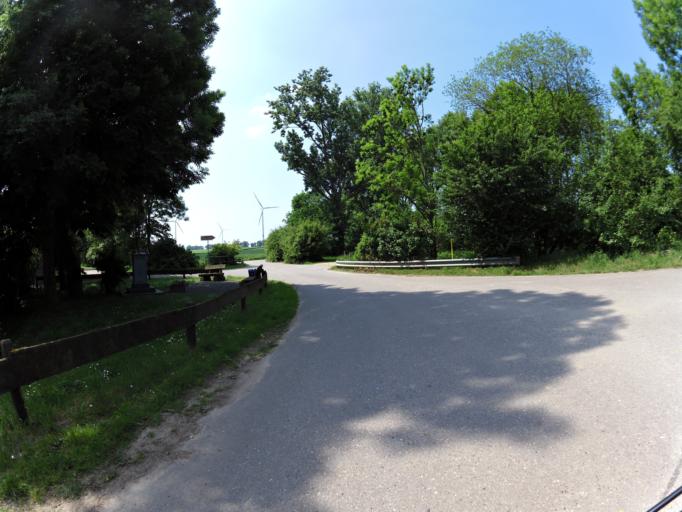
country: DE
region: North Rhine-Westphalia
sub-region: Regierungsbezirk Koln
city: Aldenhoven
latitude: 50.9153
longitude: 6.2982
